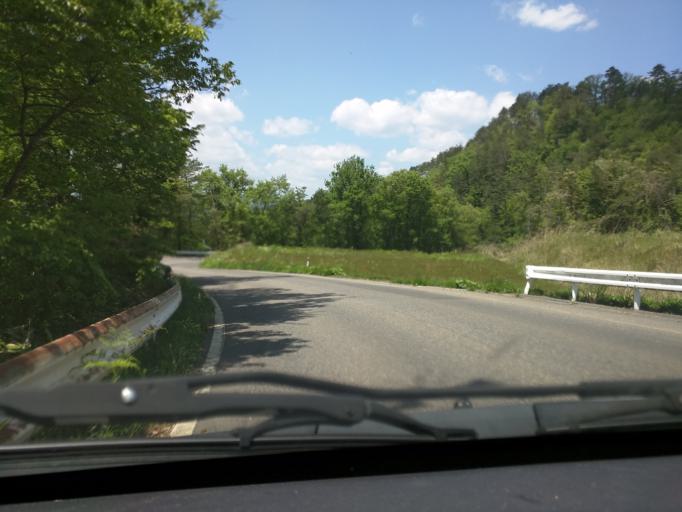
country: JP
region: Fukushima
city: Kitakata
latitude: 37.6384
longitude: 139.8100
